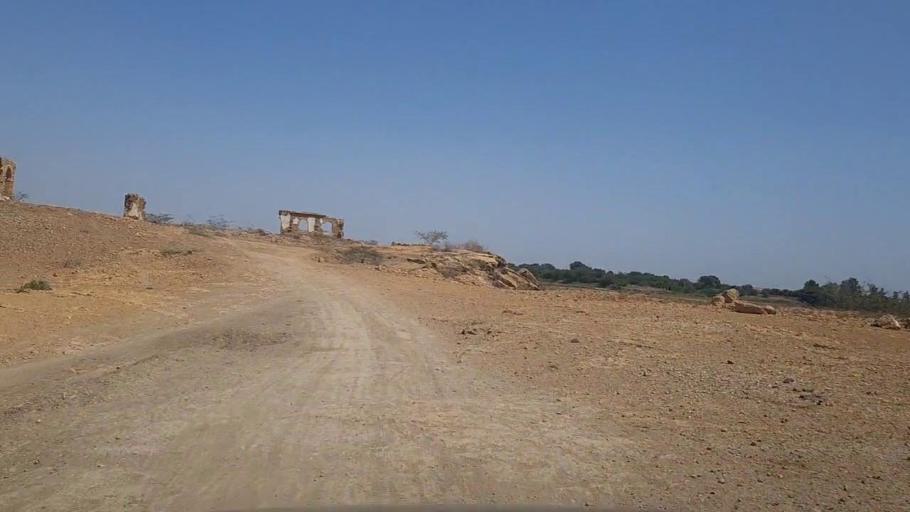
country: PK
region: Sindh
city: Thatta
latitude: 24.8071
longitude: 68.0055
